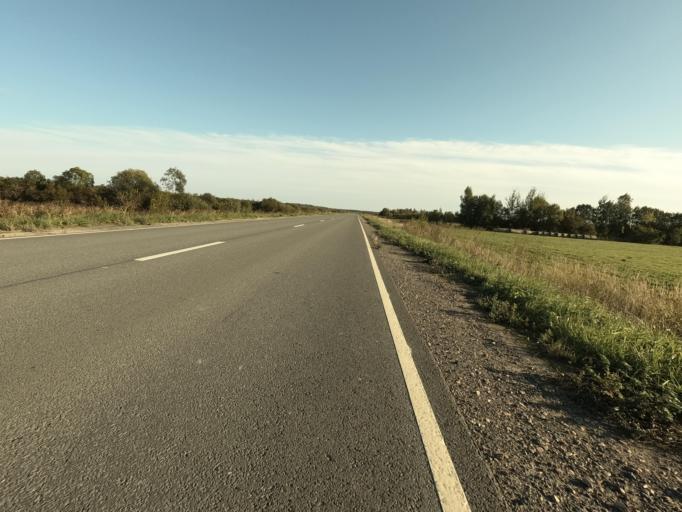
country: RU
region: St.-Petersburg
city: Sapernyy
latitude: 59.7468
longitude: 30.6433
